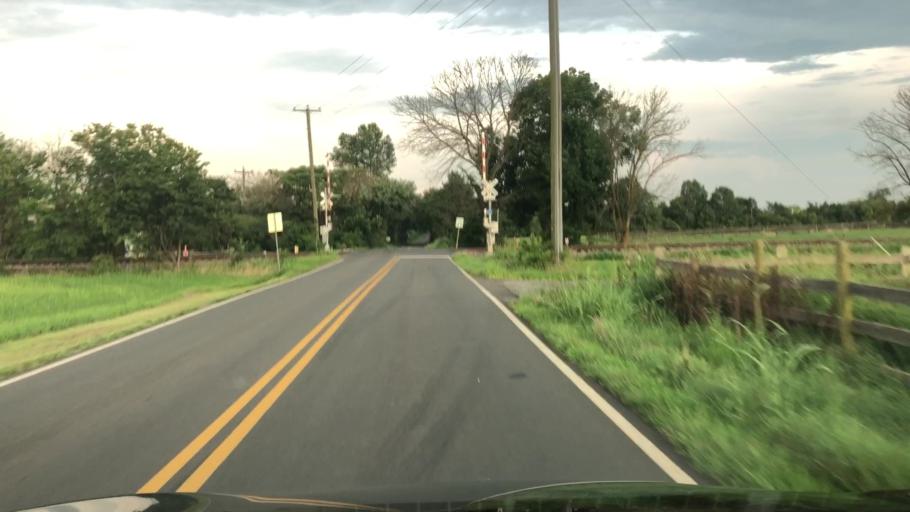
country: US
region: Virginia
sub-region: Fauquier County
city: Bealeton
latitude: 38.6025
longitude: -77.7183
